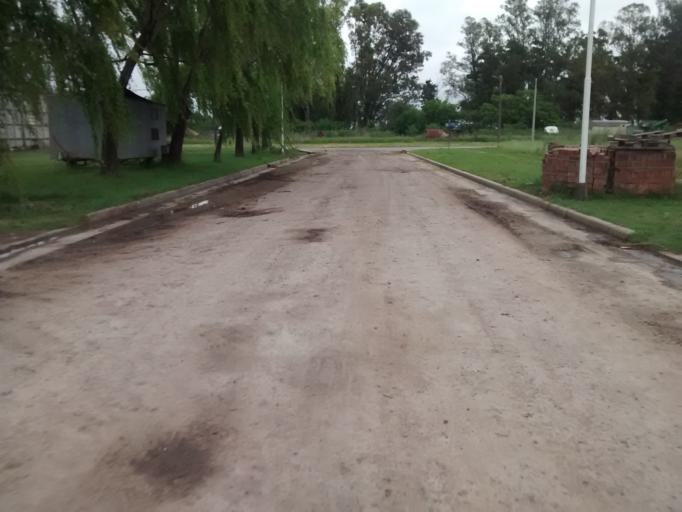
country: AR
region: Santa Fe
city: Galvez
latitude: -31.9014
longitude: -61.2808
